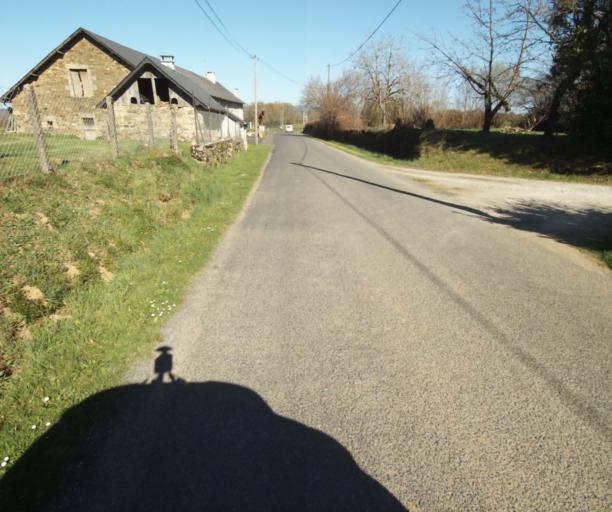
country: FR
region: Limousin
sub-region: Departement de la Correze
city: Chamboulive
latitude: 45.4400
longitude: 1.6755
